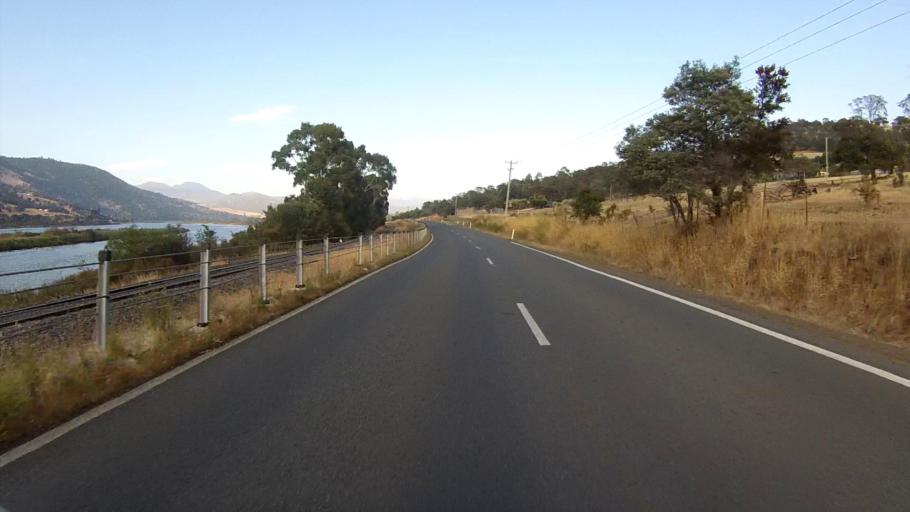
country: AU
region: Tasmania
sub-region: Glenorchy
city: Granton
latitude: -42.7512
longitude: 147.1505
